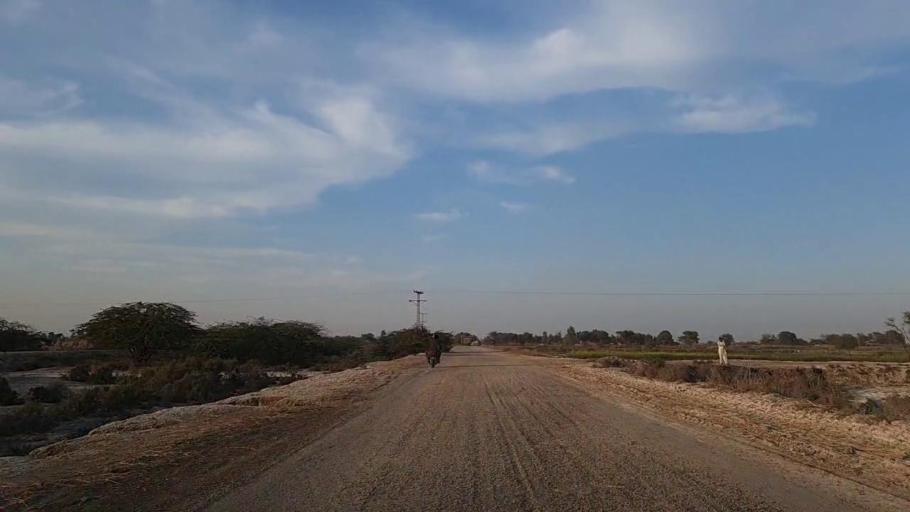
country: PK
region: Sindh
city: Bandhi
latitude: 26.5946
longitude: 68.3412
